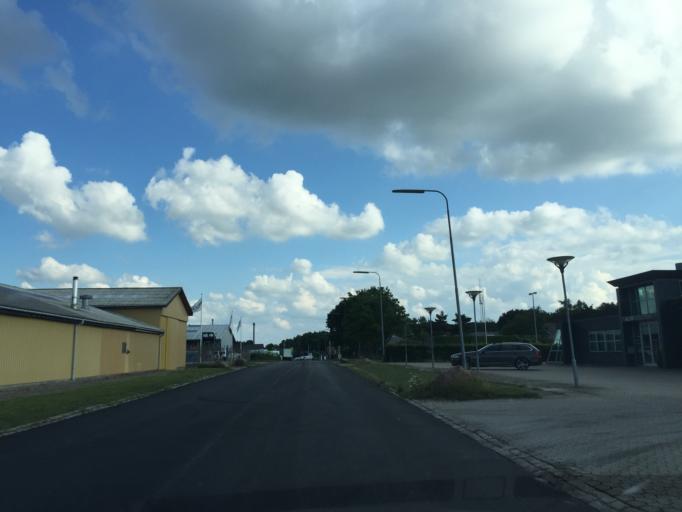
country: DK
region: South Denmark
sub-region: Odense Kommune
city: Neder Holluf
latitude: 55.3864
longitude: 10.4357
